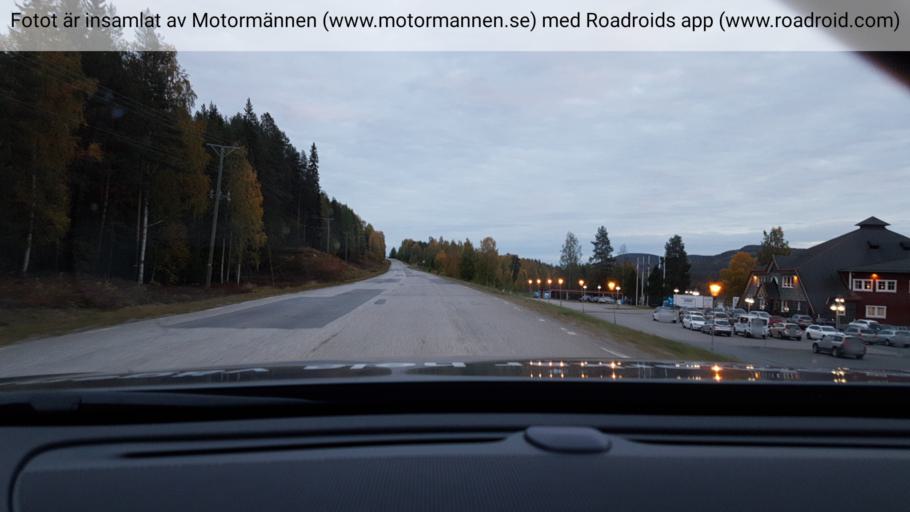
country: SE
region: Norrbotten
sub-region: Alvsbyns Kommun
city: AElvsbyn
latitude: 65.8579
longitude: 20.4216
